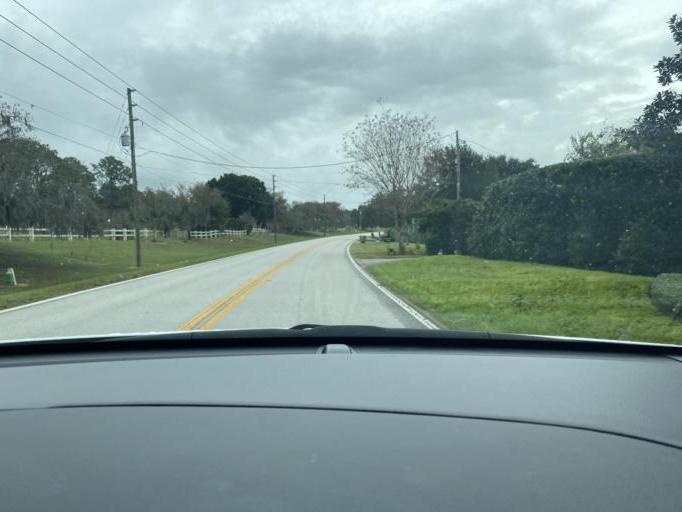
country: US
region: Florida
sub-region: Lake County
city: Minneola
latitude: 28.5887
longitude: -81.7738
